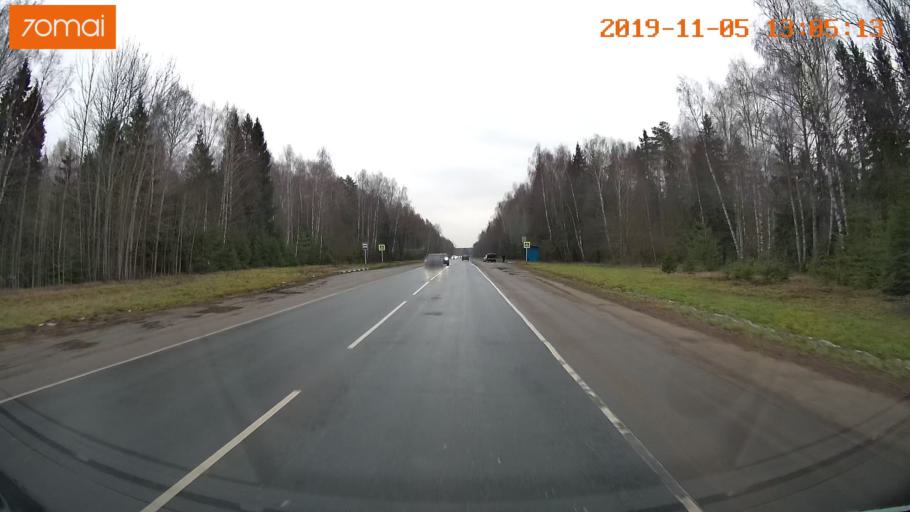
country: RU
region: Ivanovo
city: Kitovo
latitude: 56.8840
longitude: 41.2380
